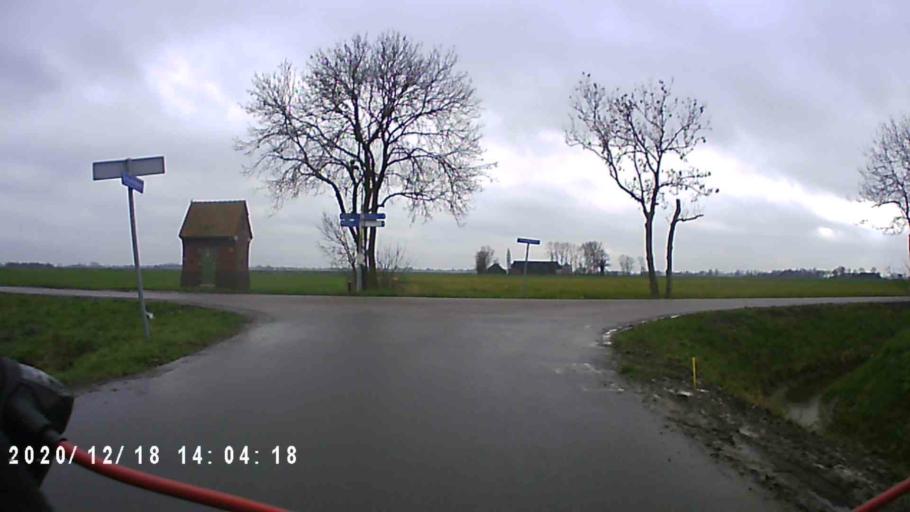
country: NL
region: Groningen
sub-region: Gemeente Bedum
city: Bedum
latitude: 53.2925
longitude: 6.6534
